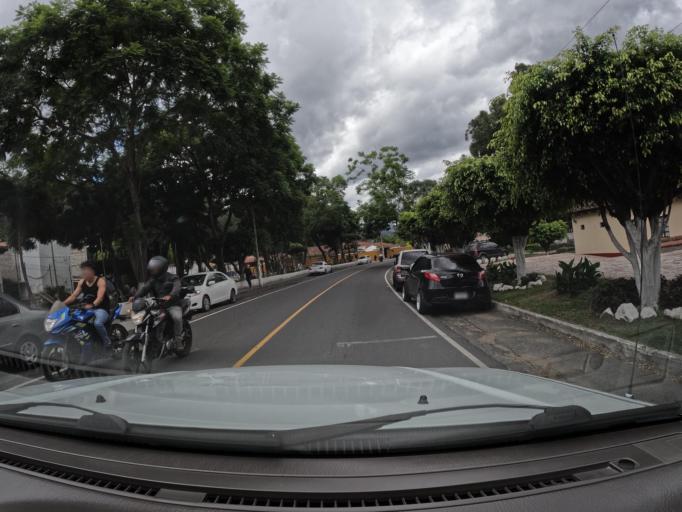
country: GT
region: Sacatepequez
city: Antigua Guatemala
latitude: 14.5657
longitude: -90.7355
